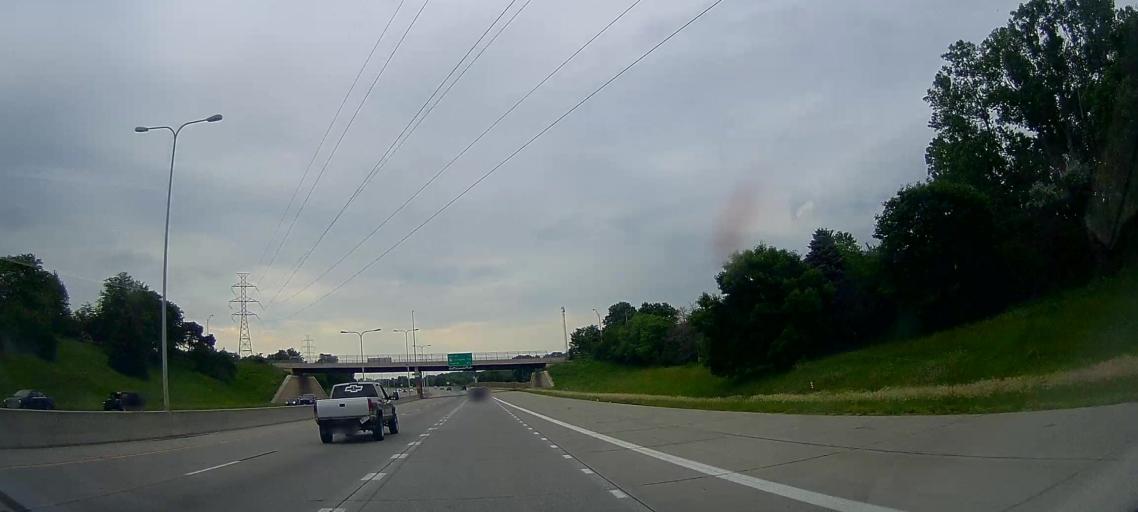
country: US
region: Nebraska
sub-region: Douglas County
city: Ralston
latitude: 41.2951
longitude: -96.0719
